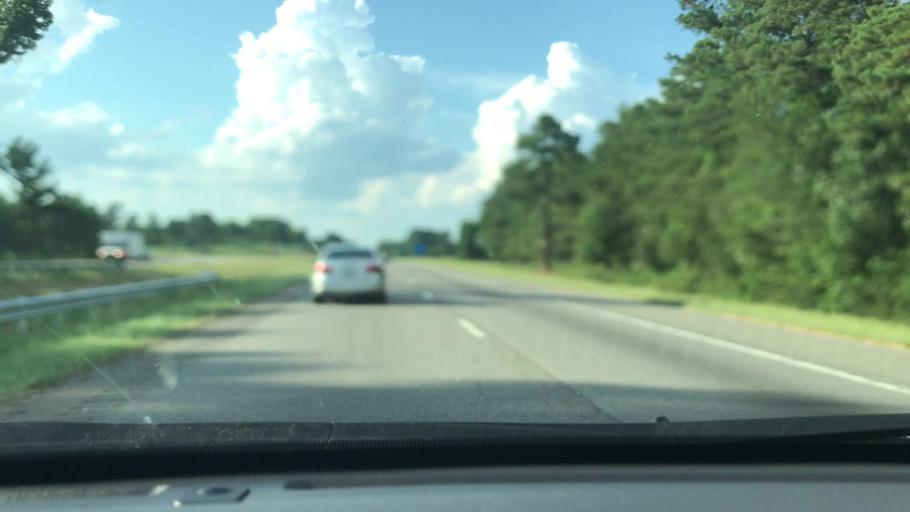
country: US
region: North Carolina
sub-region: Robeson County
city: Saint Pauls
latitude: 34.7151
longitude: -78.9973
